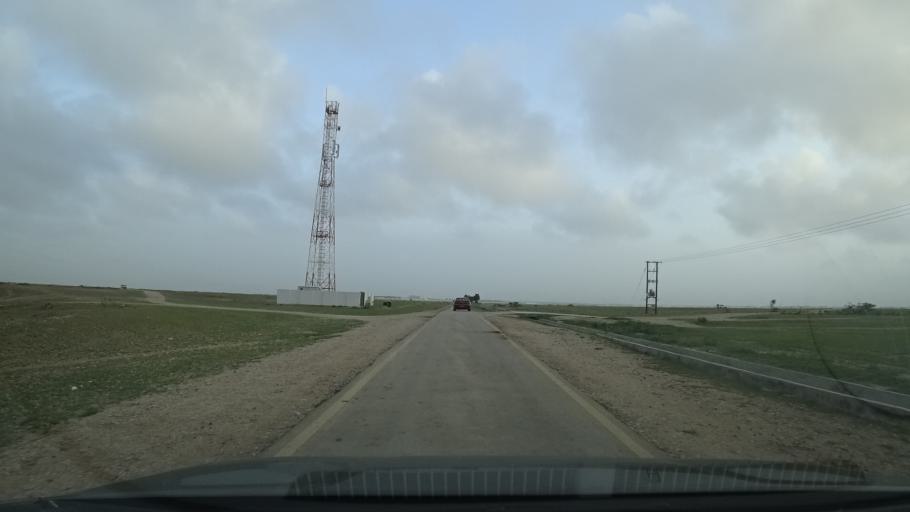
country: OM
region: Zufar
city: Salalah
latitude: 17.0875
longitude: 54.2325
